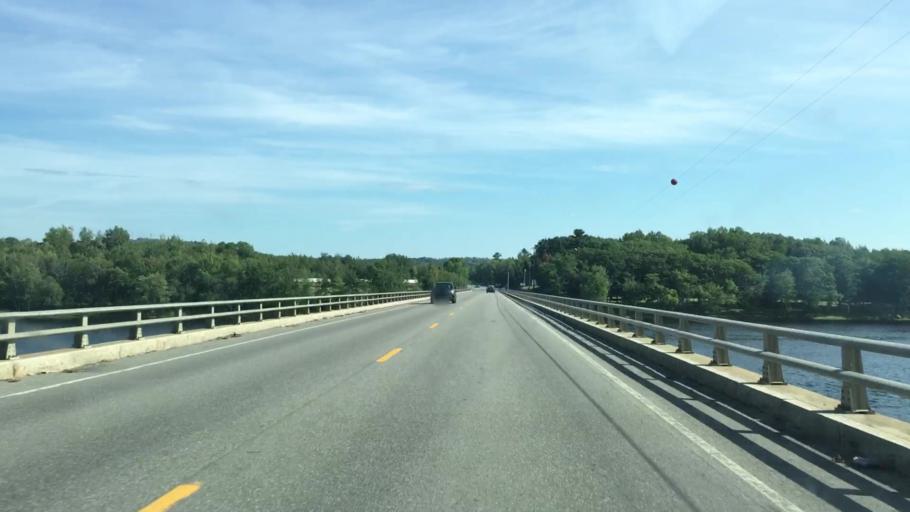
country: US
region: Maine
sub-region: Penobscot County
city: Lincoln
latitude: 45.3635
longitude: -68.5489
